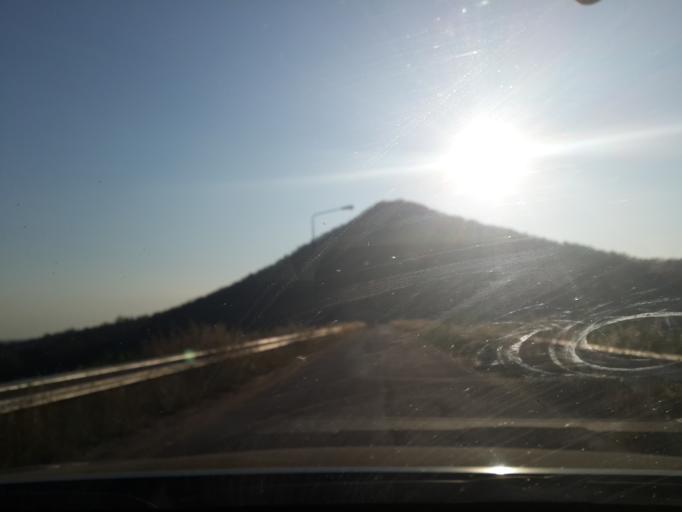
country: TH
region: Chiang Mai
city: San Sai
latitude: 18.9397
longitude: 99.1408
